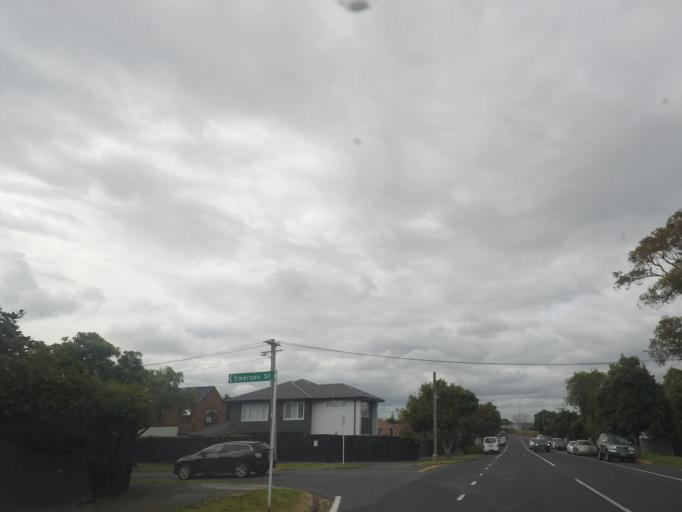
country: NZ
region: Auckland
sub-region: Auckland
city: Tamaki
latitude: -36.8680
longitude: 174.8561
